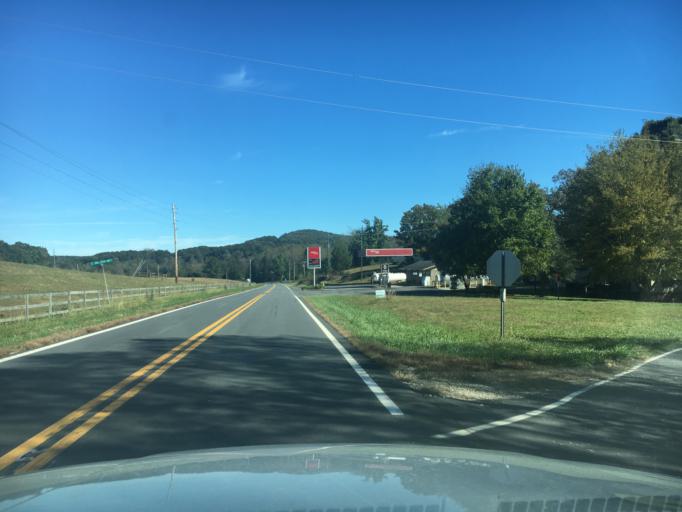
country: US
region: North Carolina
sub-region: Burke County
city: Glen Alpine
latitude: 35.6001
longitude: -81.8212
